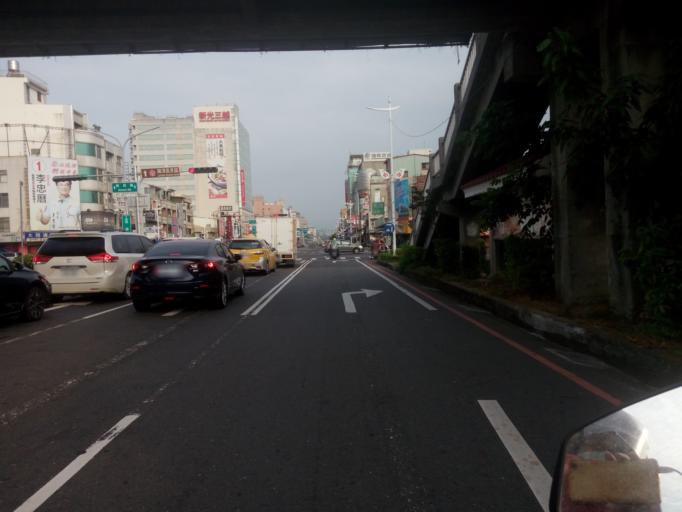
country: TW
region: Taiwan
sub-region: Chiayi
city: Jiayi Shi
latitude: 23.4728
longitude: 120.4389
